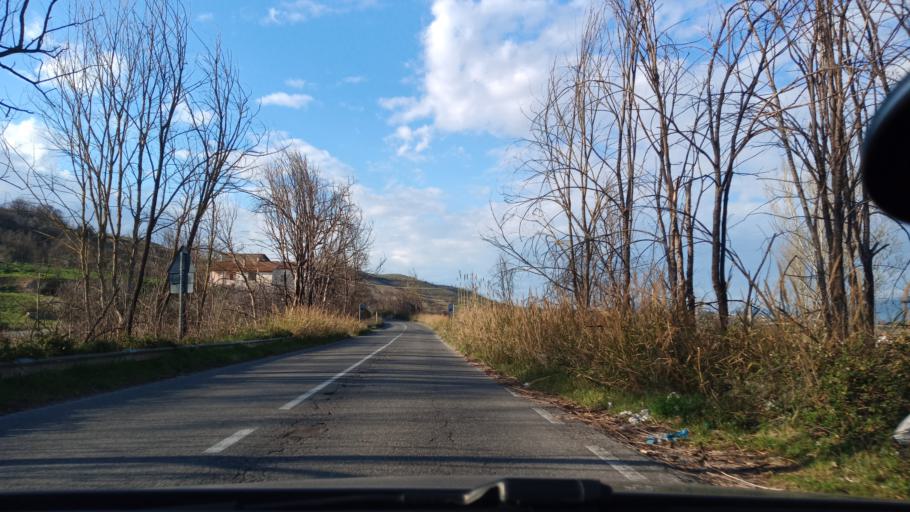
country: IT
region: Latium
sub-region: Citta metropolitana di Roma Capitale
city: Fiano Romano
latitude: 42.1856
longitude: 12.6048
